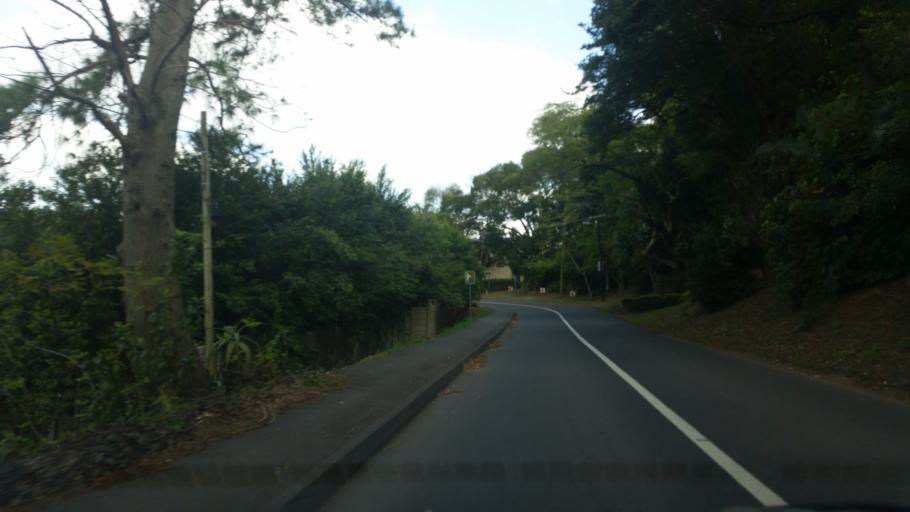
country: ZA
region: KwaZulu-Natal
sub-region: eThekwini Metropolitan Municipality
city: Berea
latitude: -29.8333
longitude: 30.9012
